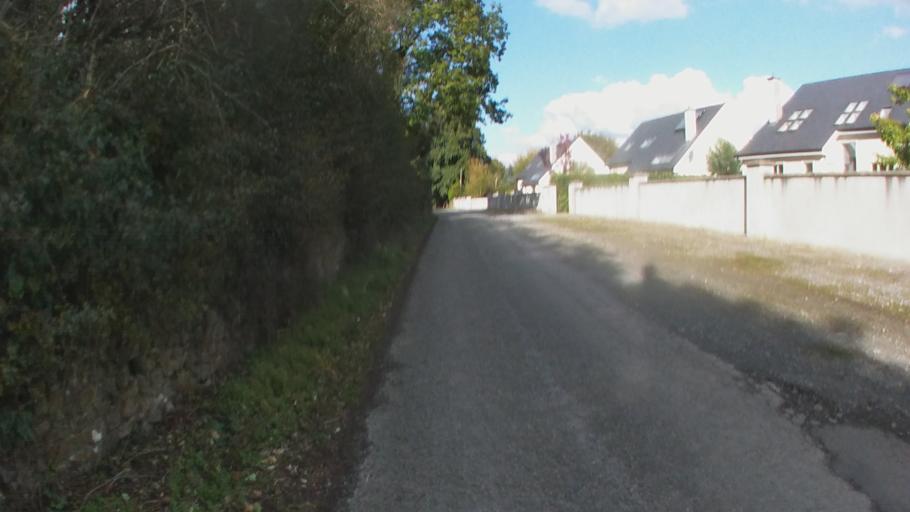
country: IE
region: Leinster
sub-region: Kilkenny
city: Kilkenny
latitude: 52.6712
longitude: -7.2357
